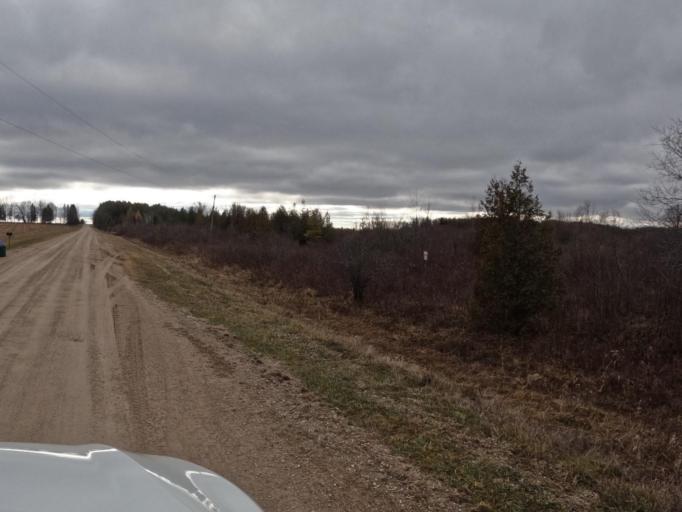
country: CA
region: Ontario
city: Shelburne
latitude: 43.9675
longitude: -80.4012
